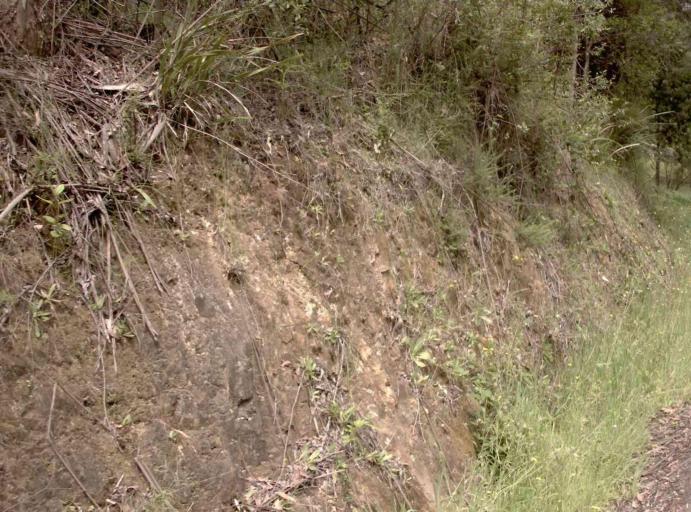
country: AU
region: Victoria
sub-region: Baw Baw
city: Warragul
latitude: -37.8899
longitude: 146.0961
